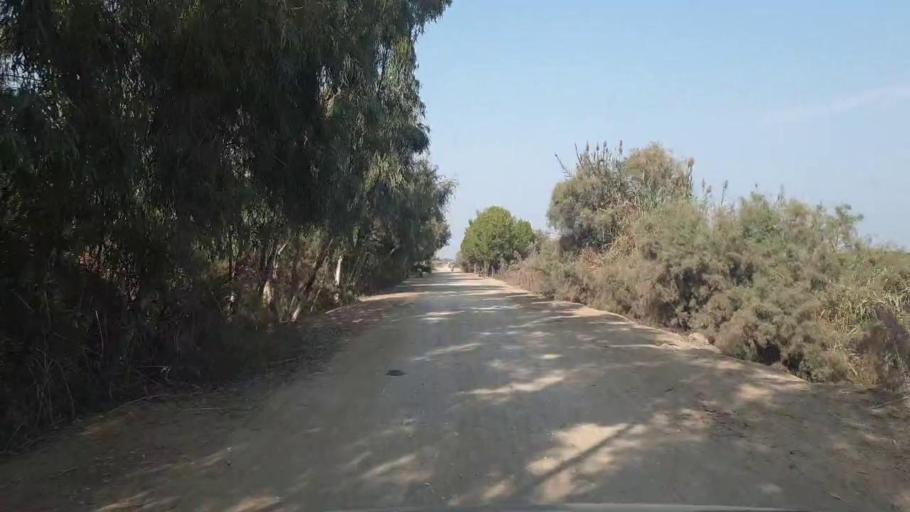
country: PK
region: Sindh
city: Tando Adam
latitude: 25.7977
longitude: 68.5923
